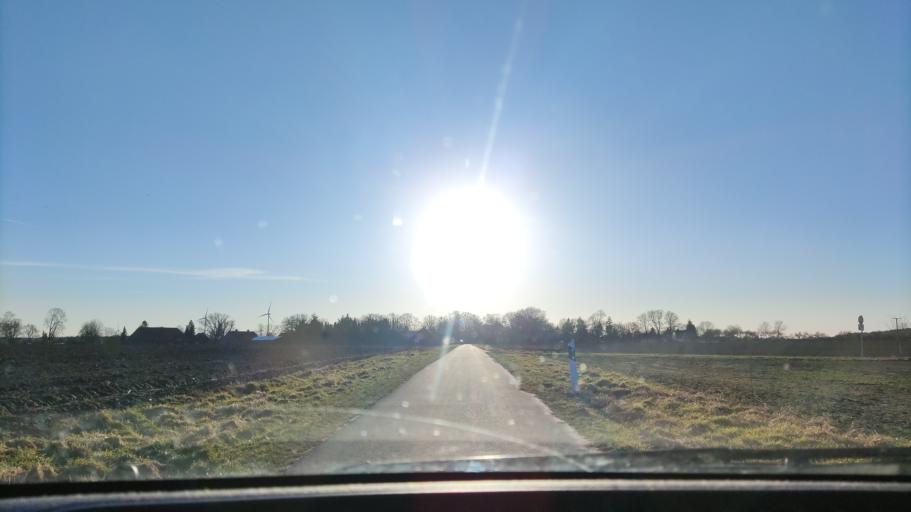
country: DE
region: Lower Saxony
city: Tosterglope
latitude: 53.2128
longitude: 10.8270
